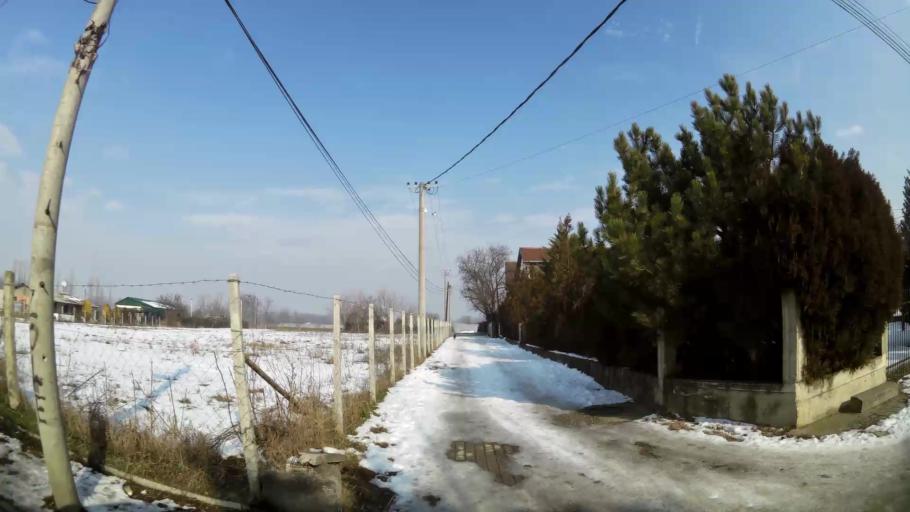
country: MK
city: Krushopek
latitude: 42.0164
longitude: 21.3761
